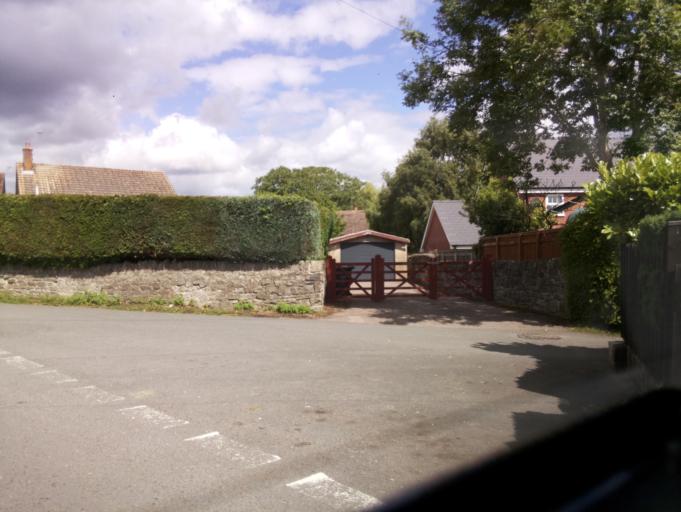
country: GB
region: England
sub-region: Gloucestershire
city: Bream
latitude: 51.7506
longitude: -2.5724
